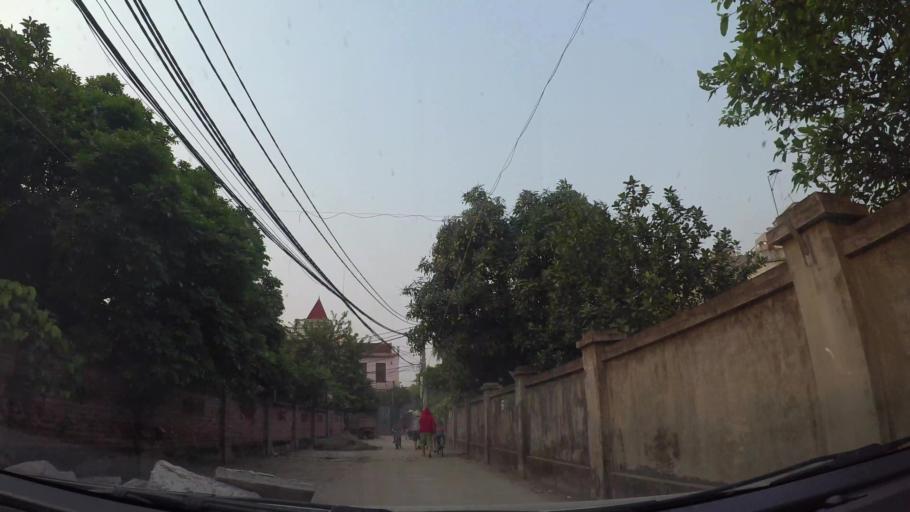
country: VN
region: Ha Noi
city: Cau Dien
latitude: 21.0059
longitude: 105.7240
